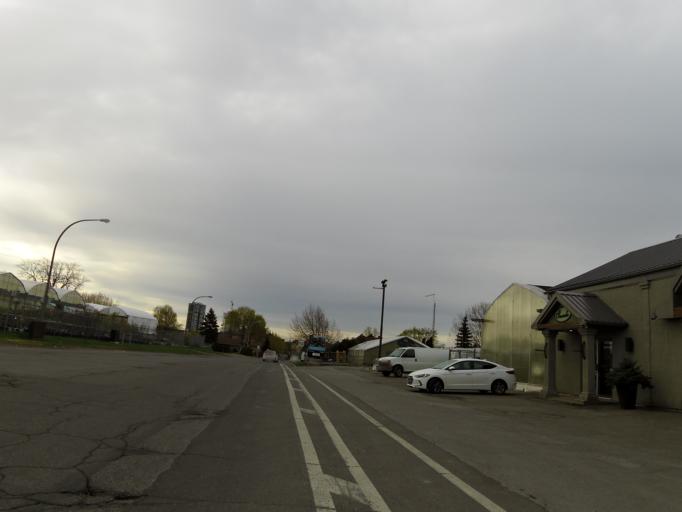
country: CA
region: Quebec
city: Dollard-Des Ormeaux
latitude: 45.5219
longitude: -73.7813
